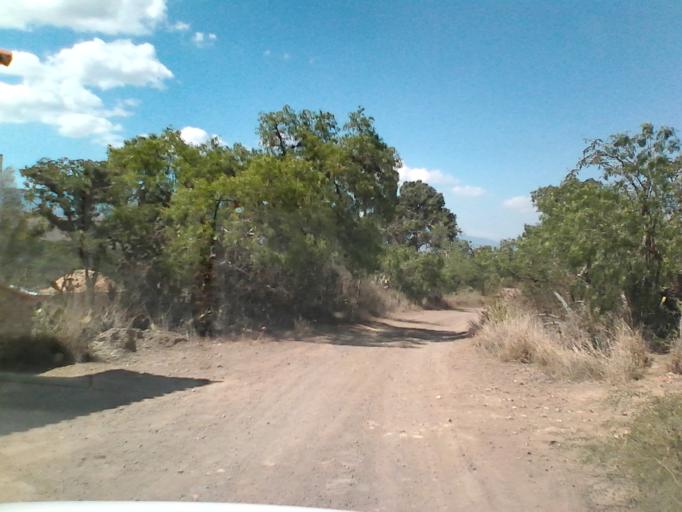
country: CO
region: Boyaca
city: Sachica
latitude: 5.6081
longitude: -73.5577
